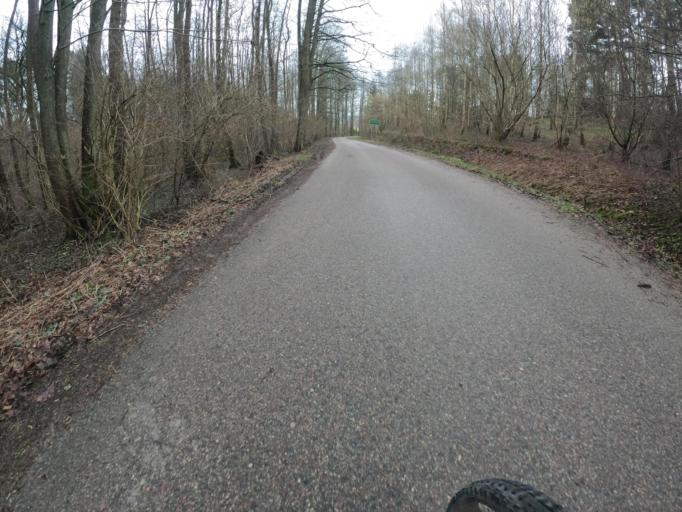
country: PL
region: West Pomeranian Voivodeship
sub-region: Powiat slawienski
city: Slawno
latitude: 54.2555
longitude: 16.6581
